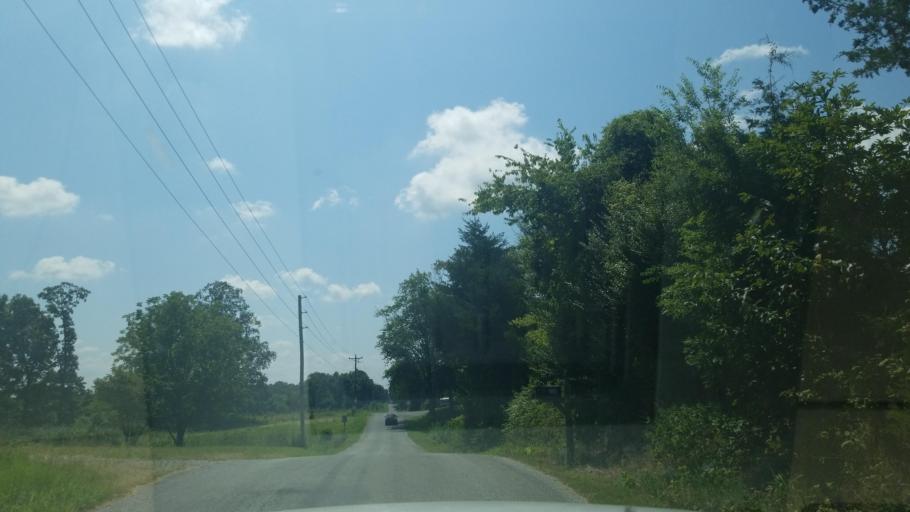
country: US
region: Illinois
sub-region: Saline County
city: Harrisburg
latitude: 37.7951
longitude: -88.6240
